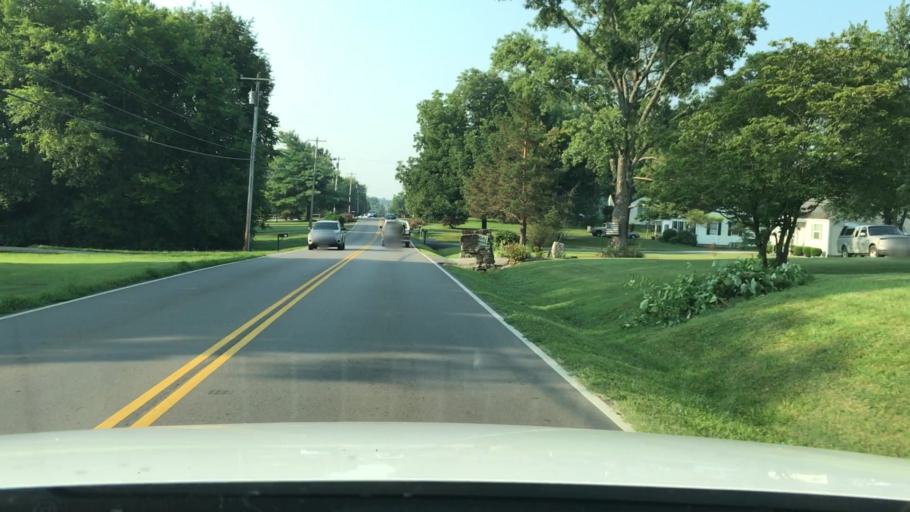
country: US
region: Tennessee
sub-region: Sumner County
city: Gallatin
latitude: 36.3753
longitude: -86.4679
